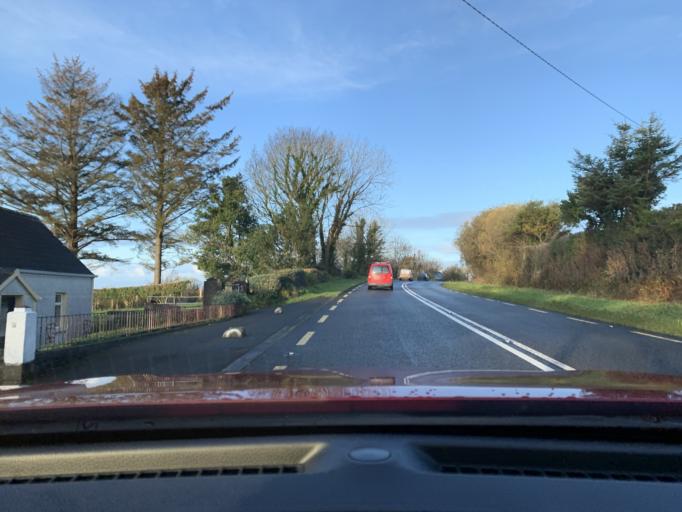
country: IE
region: Connaught
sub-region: Sligo
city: Sligo
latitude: 54.3540
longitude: -8.5121
